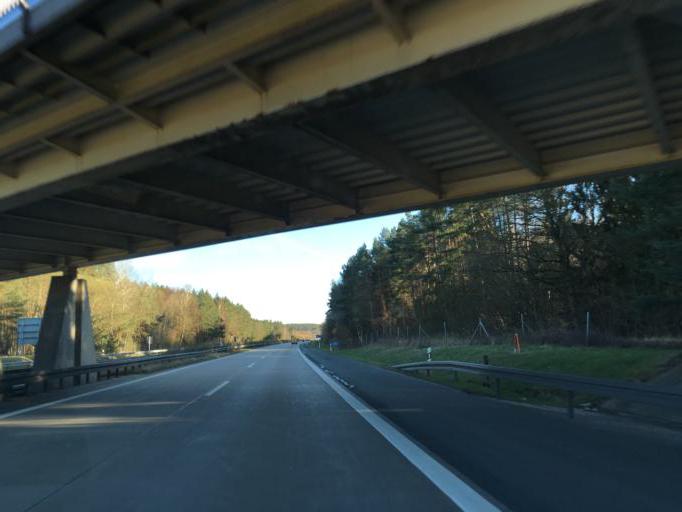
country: DE
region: Mecklenburg-Vorpommern
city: Lalendorf
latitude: 53.7735
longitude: 12.3208
